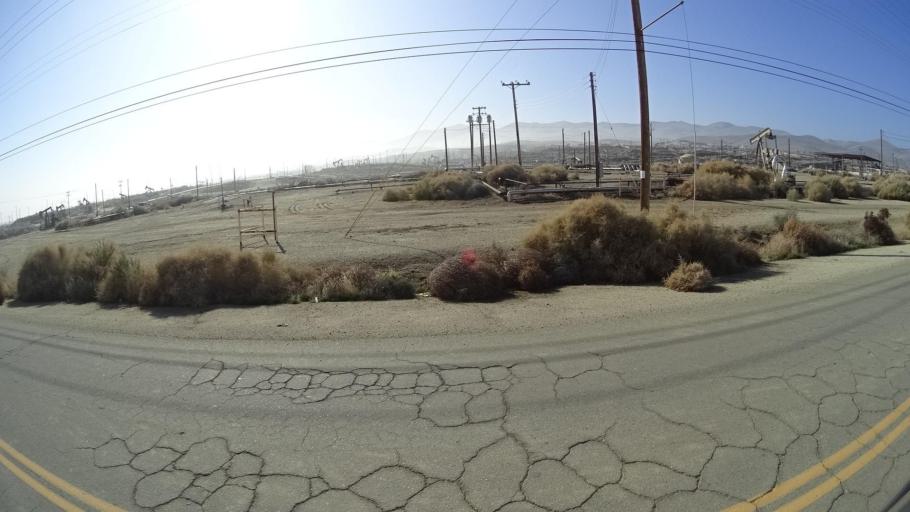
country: US
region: California
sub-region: Kern County
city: Taft Heights
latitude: 35.2230
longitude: -119.6127
